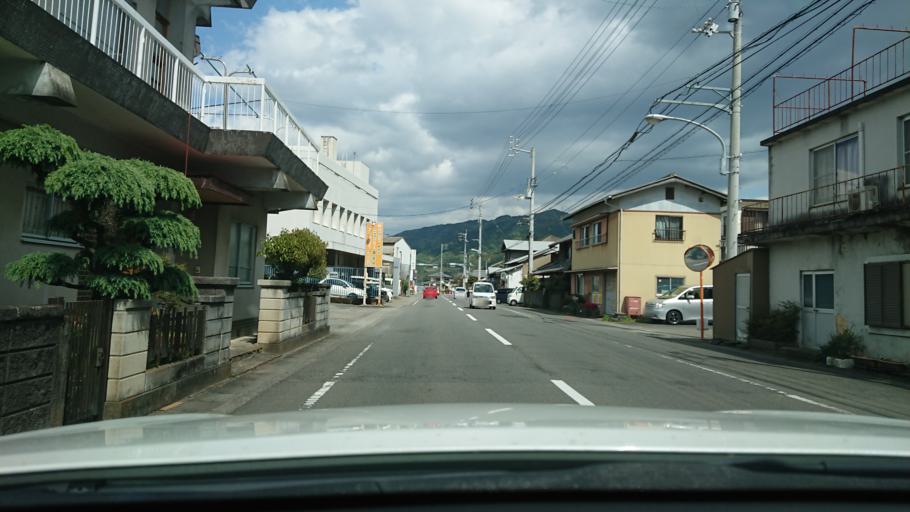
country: JP
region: Tokushima
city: Komatsushimacho
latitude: 33.9316
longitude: 134.5044
